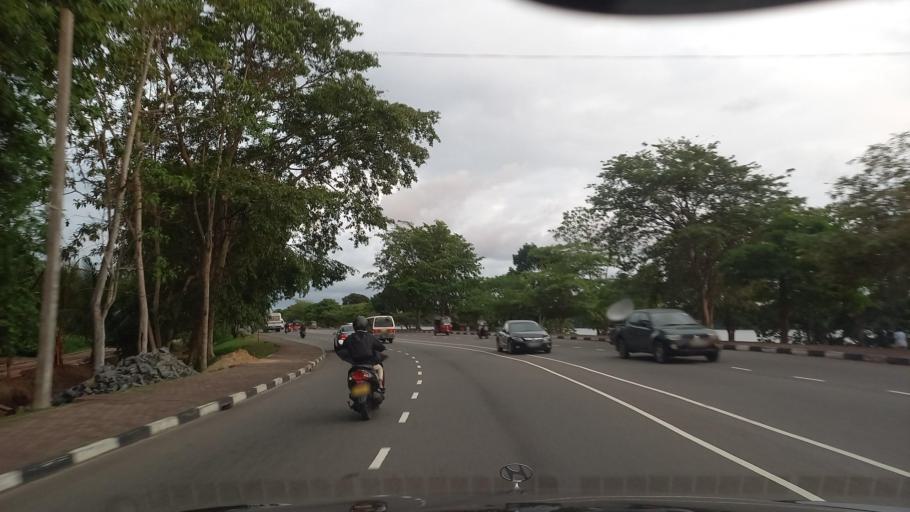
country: LK
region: Western
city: Battaramulla South
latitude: 6.8898
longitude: 79.9208
